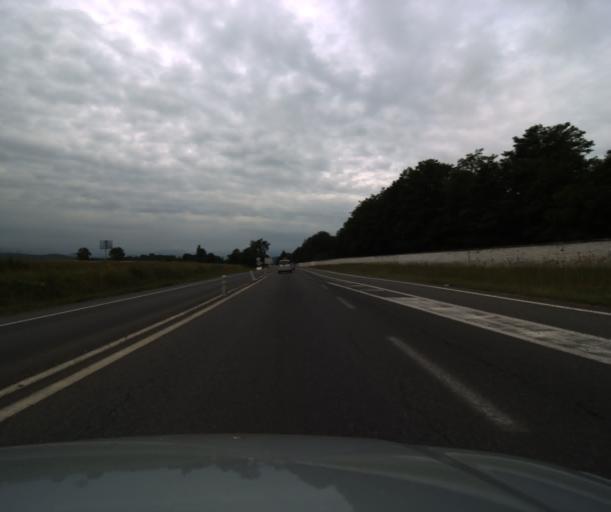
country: FR
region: Midi-Pyrenees
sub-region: Departement des Hautes-Pyrenees
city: Juillan
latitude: 43.1811
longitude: 0.0108
